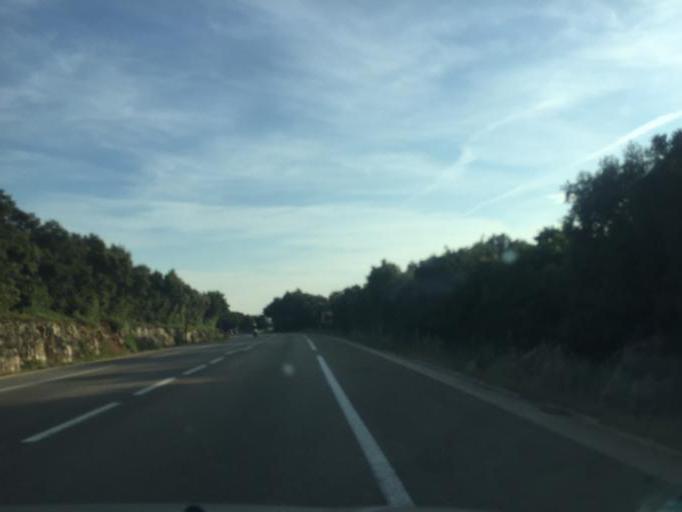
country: FR
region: Languedoc-Roussillon
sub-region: Departement du Gard
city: Tavel
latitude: 44.0132
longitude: 4.7365
